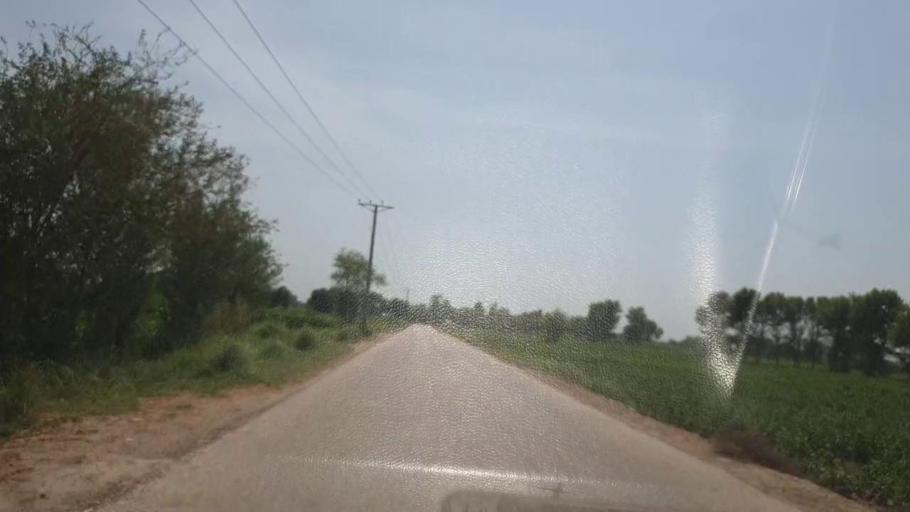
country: PK
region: Sindh
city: Bozdar
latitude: 27.0642
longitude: 68.5867
